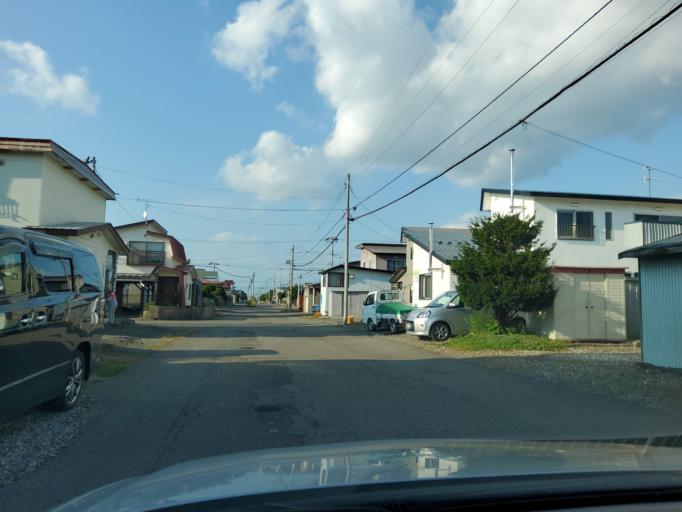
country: JP
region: Hokkaido
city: Obihiro
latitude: 42.9108
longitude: 143.1624
